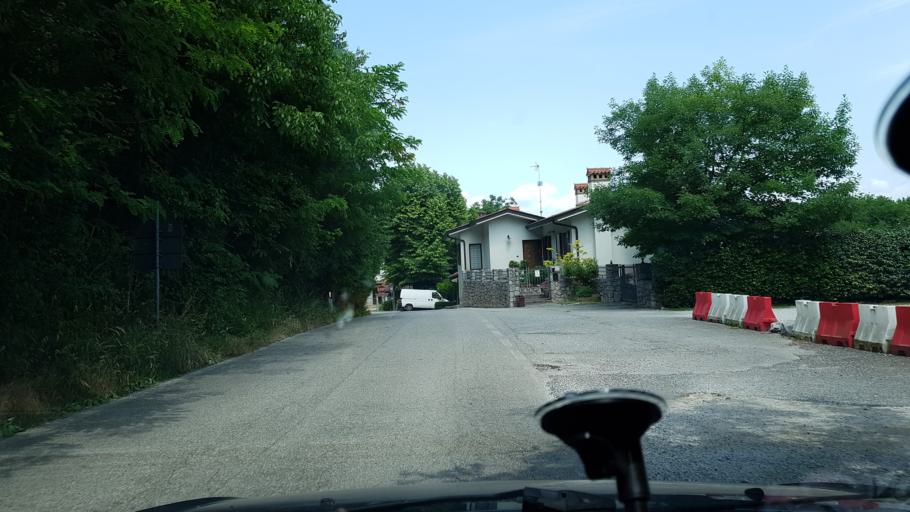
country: IT
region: Friuli Venezia Giulia
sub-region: Provincia di Gorizia
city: Savogna d'Isonzo
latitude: 45.8971
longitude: 13.5698
